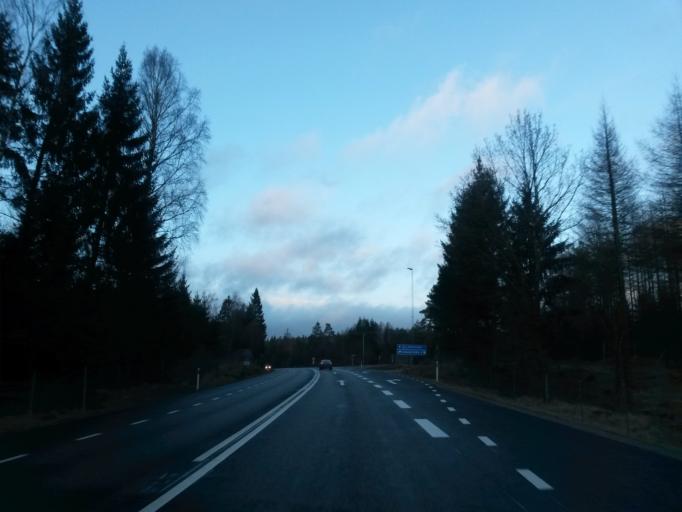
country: SE
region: Halland
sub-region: Halmstads Kommun
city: Oskarstrom
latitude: 56.7853
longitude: 12.9585
